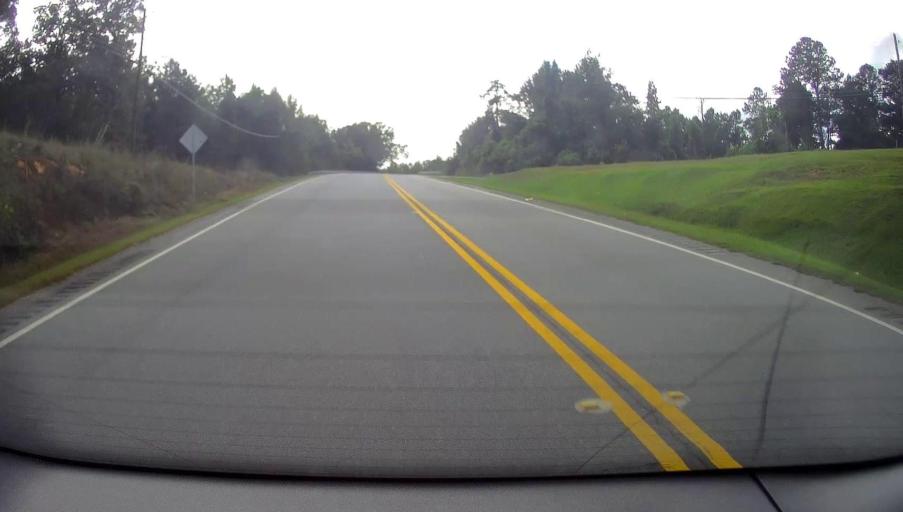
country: US
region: Georgia
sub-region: Baldwin County
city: Milledgeville
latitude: 33.0626
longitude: -83.2744
